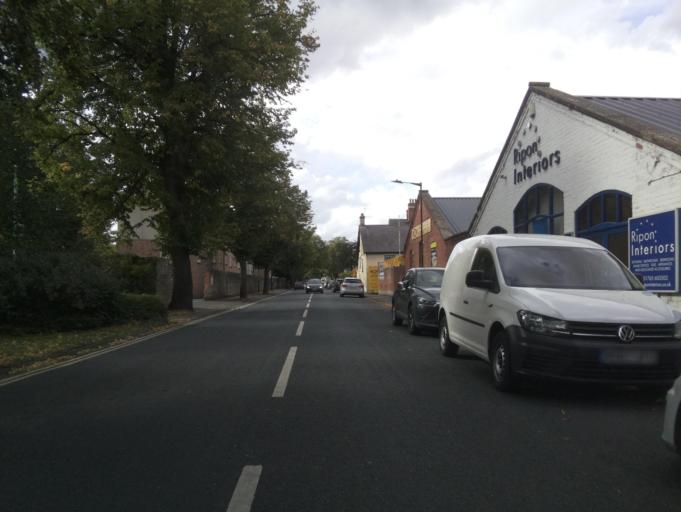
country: GB
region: England
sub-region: North Yorkshire
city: Ripon
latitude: 54.1323
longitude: -1.5165
